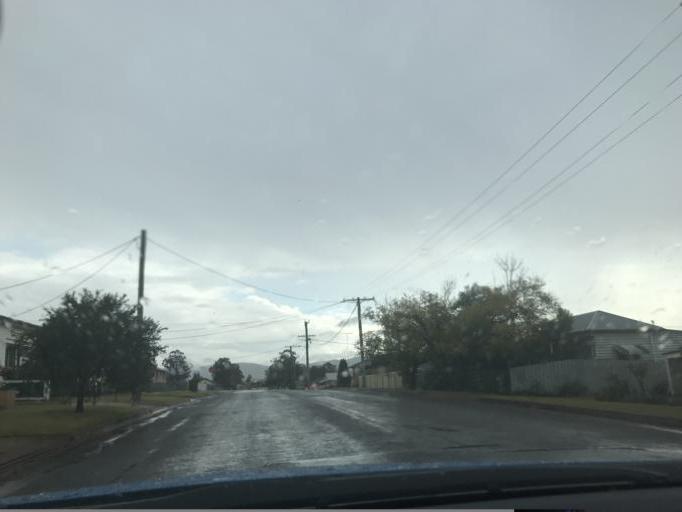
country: AU
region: New South Wales
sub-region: Cessnock
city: Cessnock
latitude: -32.8257
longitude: 151.3503
